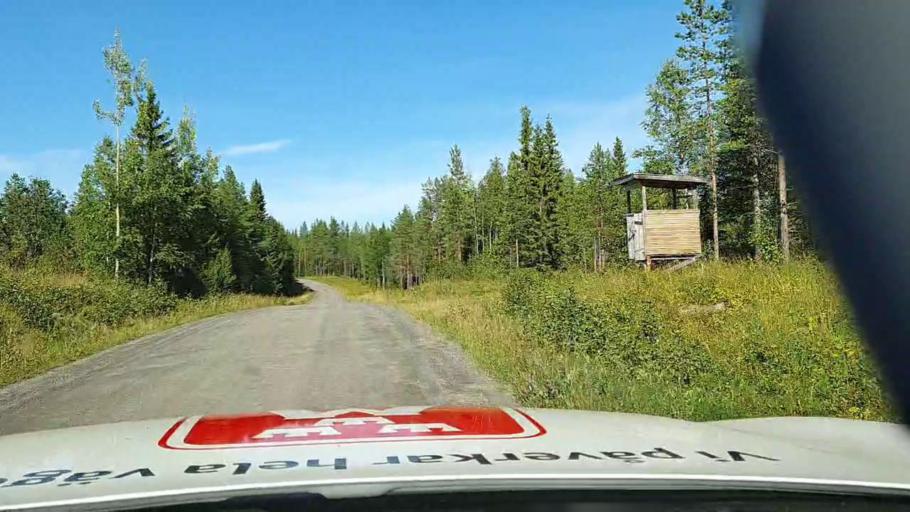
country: SE
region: Jaemtland
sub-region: OEstersunds Kommun
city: Lit
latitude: 63.7627
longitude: 14.6620
